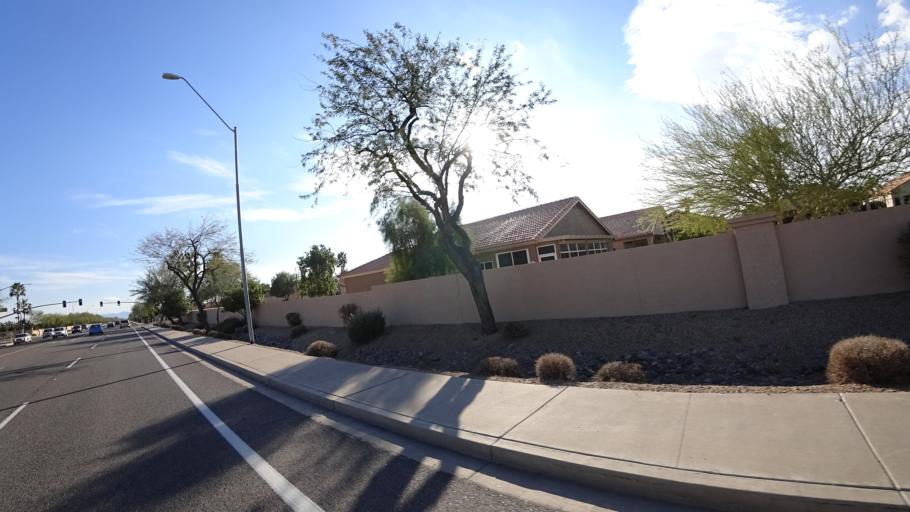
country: US
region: Arizona
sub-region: Maricopa County
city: Sun City
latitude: 33.6648
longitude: -112.2551
